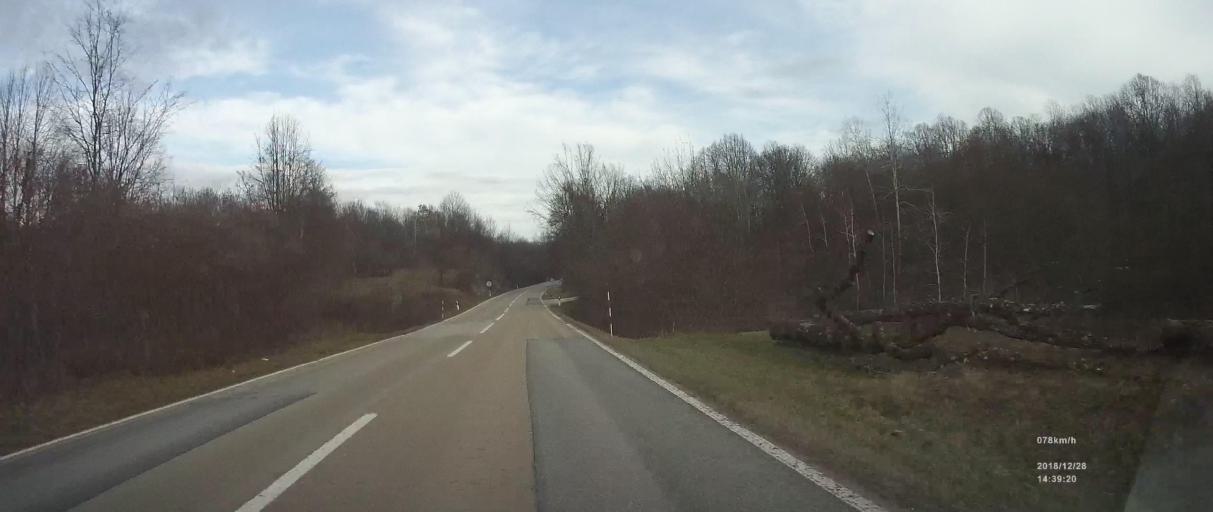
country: SI
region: Crnomelj
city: Crnomelj
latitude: 45.4272
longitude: 15.2306
